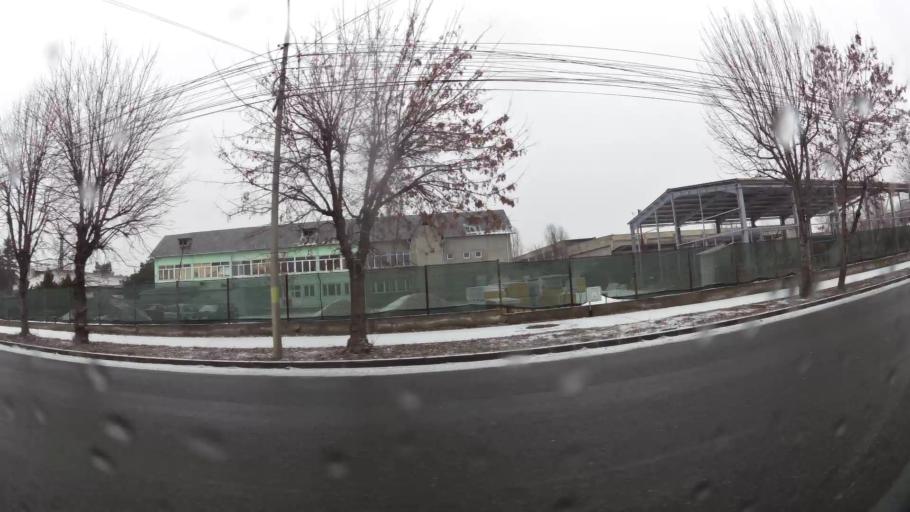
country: RO
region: Dambovita
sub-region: Municipiul Targoviste
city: Targoviste
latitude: 44.9136
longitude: 25.4434
